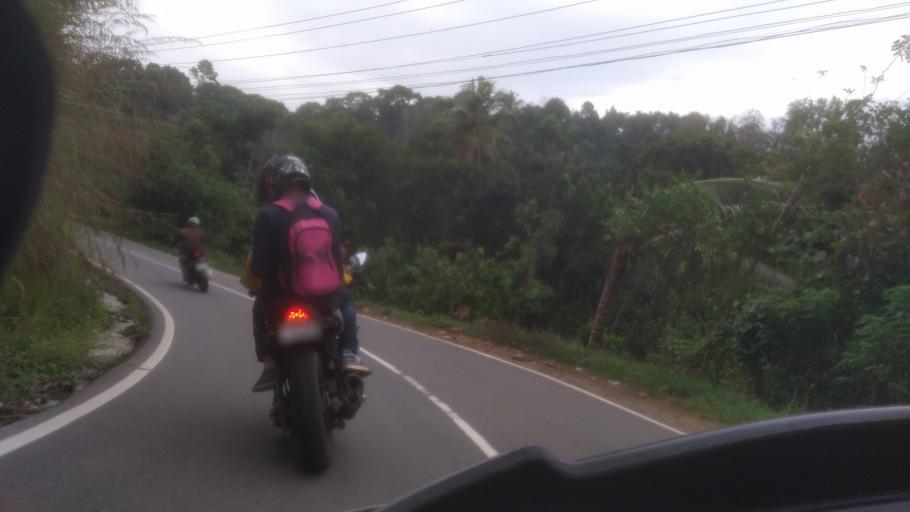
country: IN
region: Kerala
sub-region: Idukki
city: Idukki
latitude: 9.9474
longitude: 77.0134
